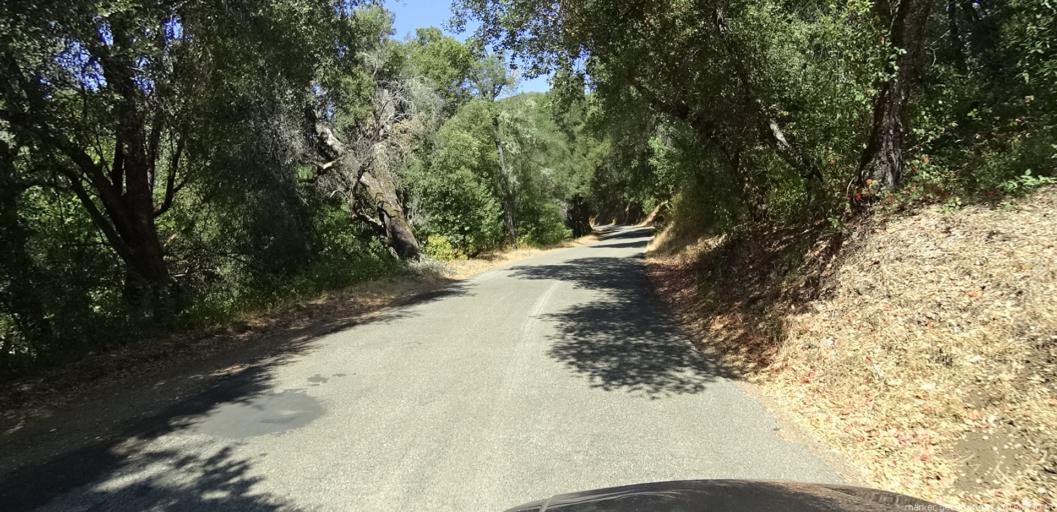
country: US
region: California
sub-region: Monterey County
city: King City
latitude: 36.0127
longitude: -121.4106
